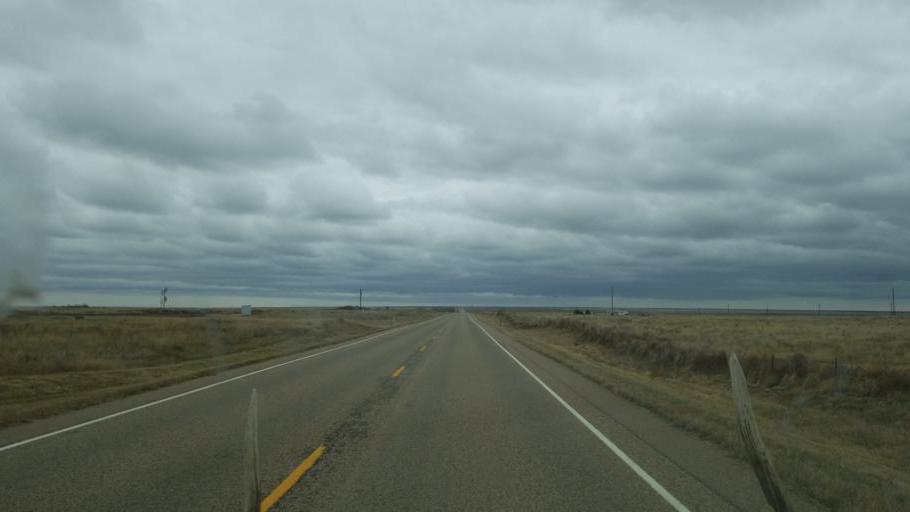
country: US
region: Colorado
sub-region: Kiowa County
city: Eads
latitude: 38.7794
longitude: -102.7243
